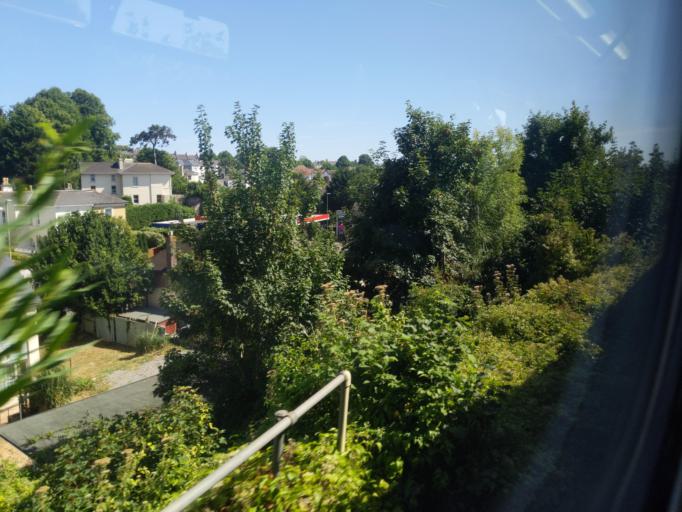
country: GB
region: England
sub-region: Borough of Torbay
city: Torquay
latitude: 50.4699
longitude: -3.5451
